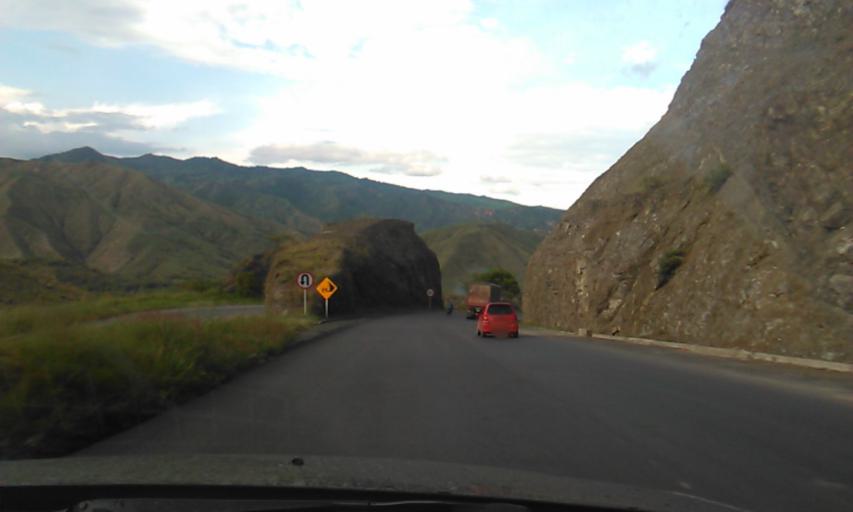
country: CO
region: Valle del Cauca
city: Yotoco
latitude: 3.8940
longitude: -76.3883
